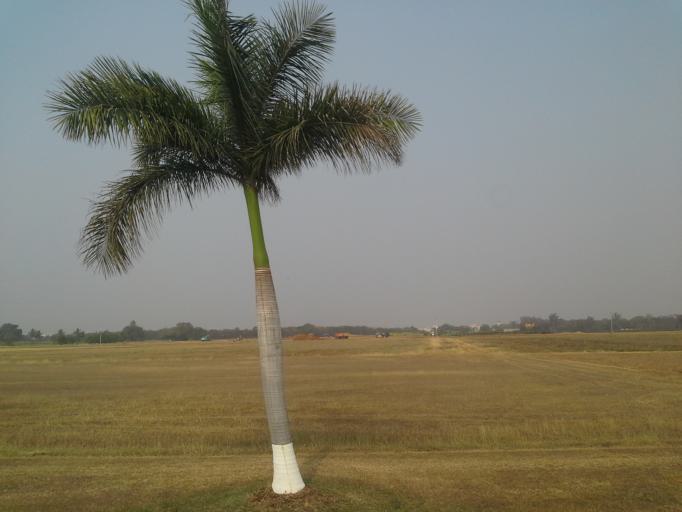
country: IN
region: Telangana
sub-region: Medak
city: Patancheru
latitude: 17.5148
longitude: 78.2760
